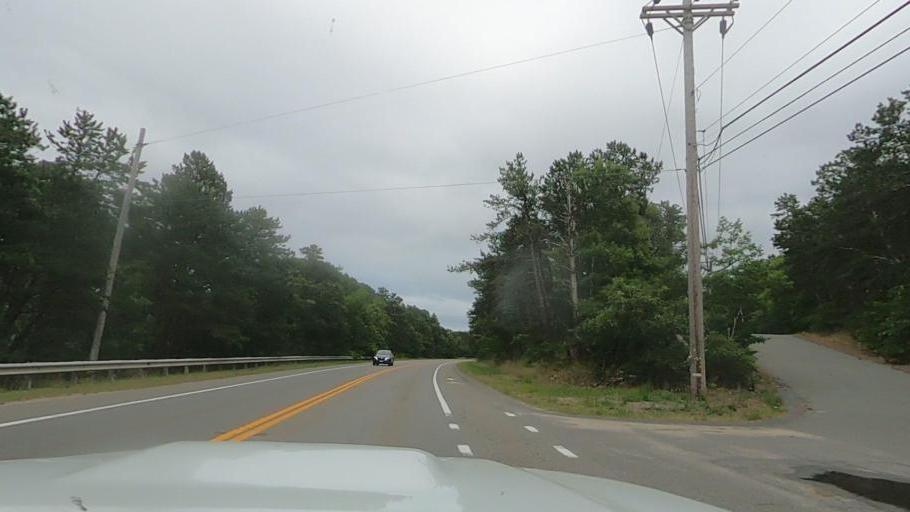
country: US
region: Massachusetts
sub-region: Barnstable County
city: Truro
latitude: 41.9716
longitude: -70.0308
